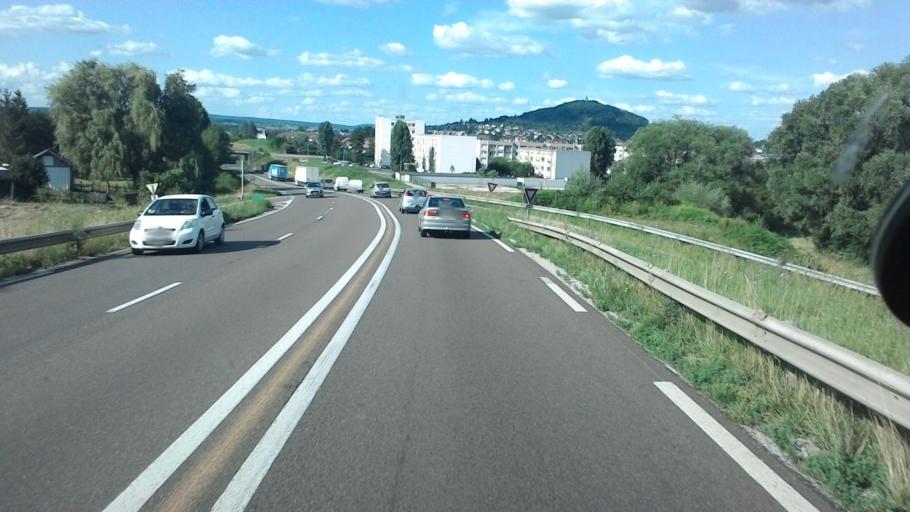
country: FR
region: Franche-Comte
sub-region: Departement de la Haute-Saone
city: Noidans-les-Vesoul
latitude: 47.6096
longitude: 6.1321
